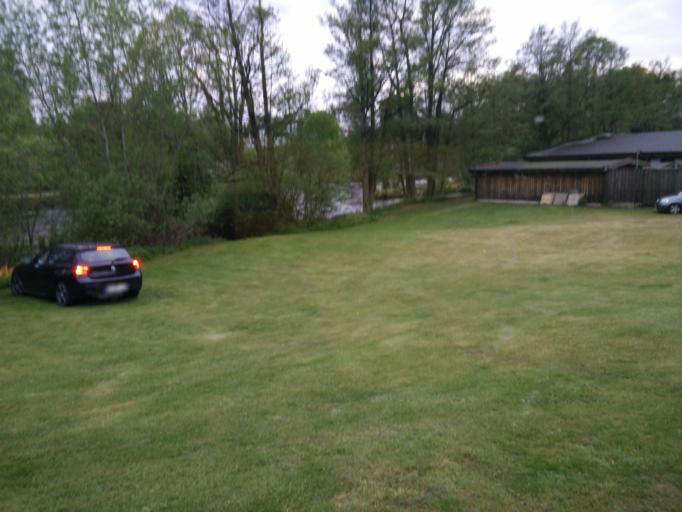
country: SE
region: Blekinge
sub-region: Karlshamns Kommun
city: Morrum
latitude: 56.1921
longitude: 14.7512
